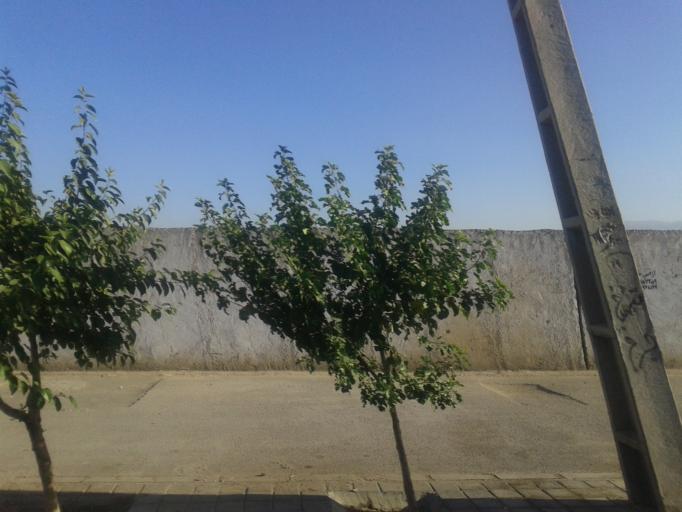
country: IR
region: Tehran
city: Rey
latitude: 35.6164
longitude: 51.3546
